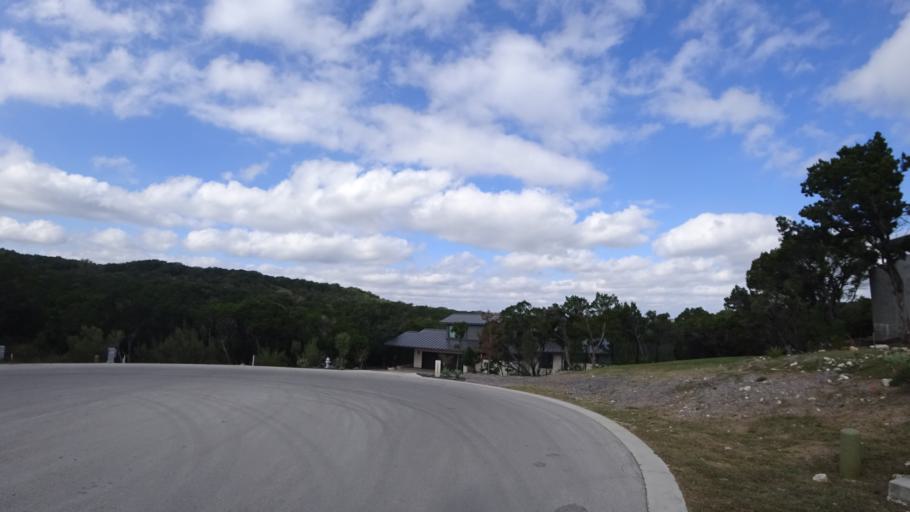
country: US
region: Texas
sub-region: Travis County
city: Bee Cave
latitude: 30.2556
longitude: -97.9291
